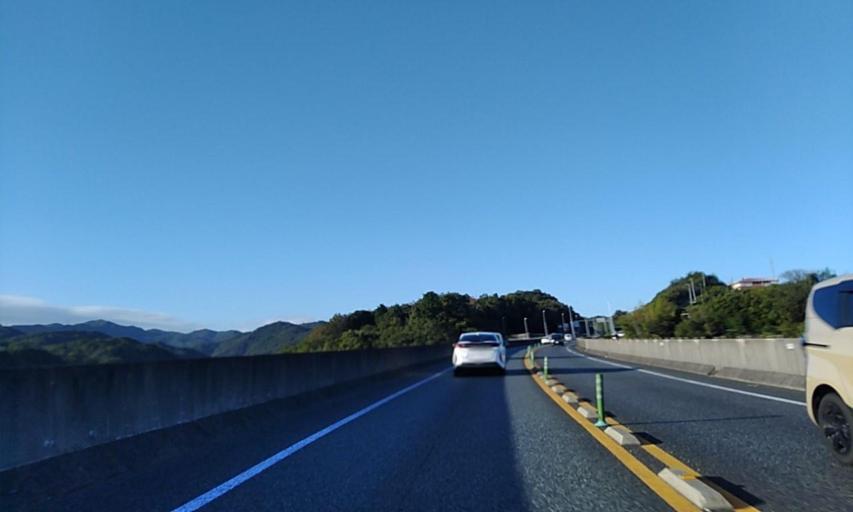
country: JP
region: Wakayama
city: Iwade
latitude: 34.3403
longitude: 135.2479
